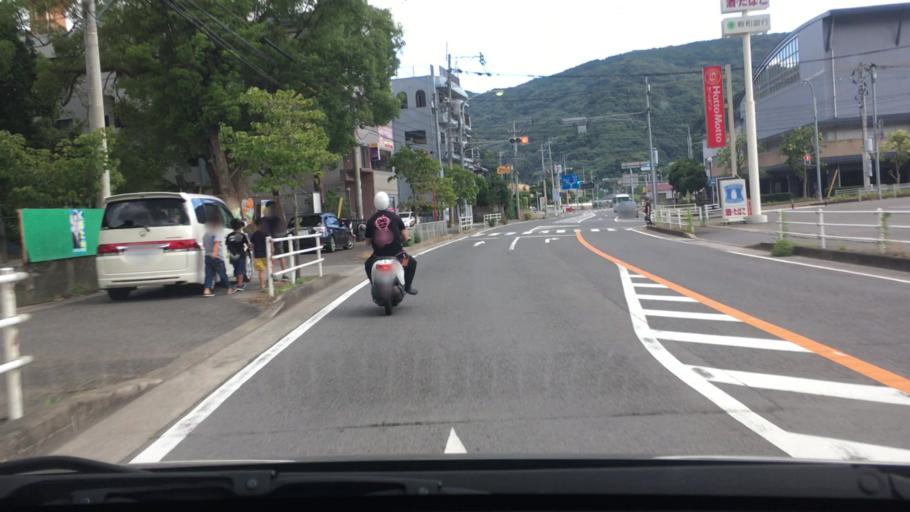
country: JP
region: Nagasaki
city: Togitsu
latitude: 32.8290
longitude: 129.7834
